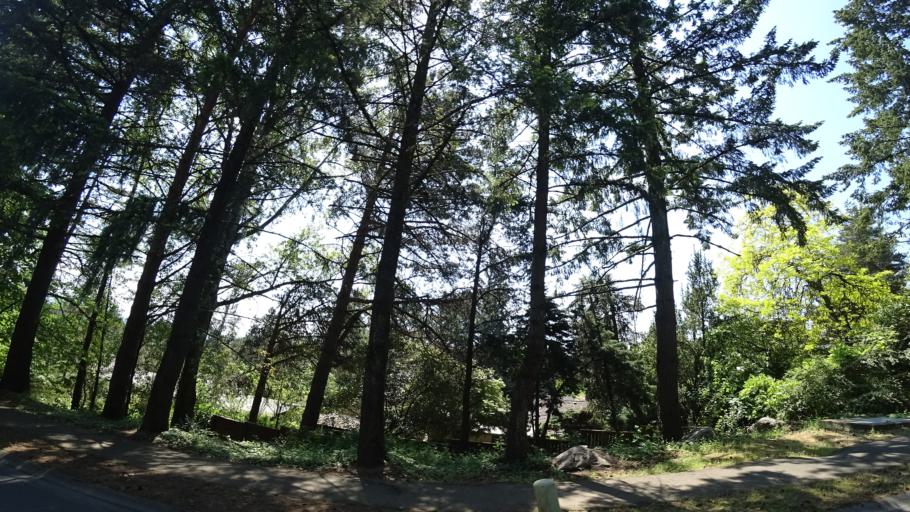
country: US
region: Oregon
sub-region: Clackamas County
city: Lake Oswego
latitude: 45.4338
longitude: -122.7117
